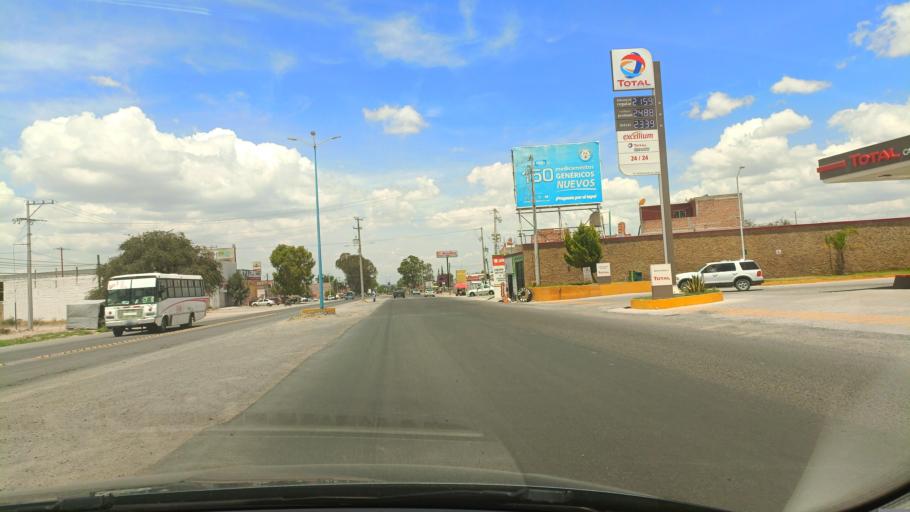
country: MX
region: Guanajuato
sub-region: San Luis de la Paz
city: San Ignacio
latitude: 21.2939
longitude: -100.5355
